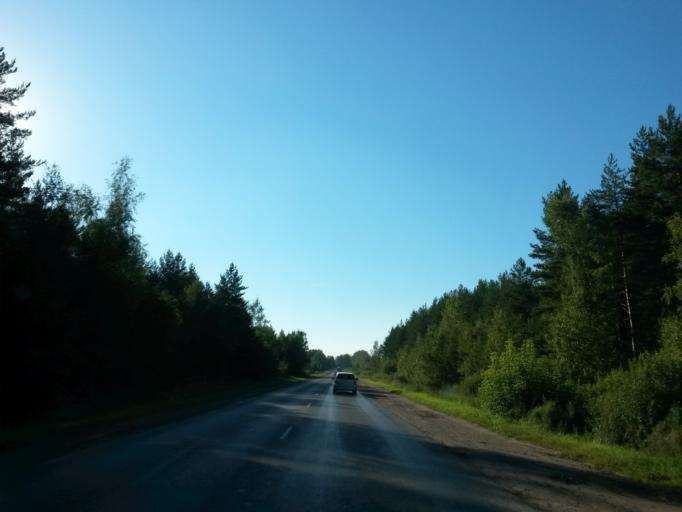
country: RU
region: Ivanovo
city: Novo-Talitsy
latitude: 57.0221
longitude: 40.7698
